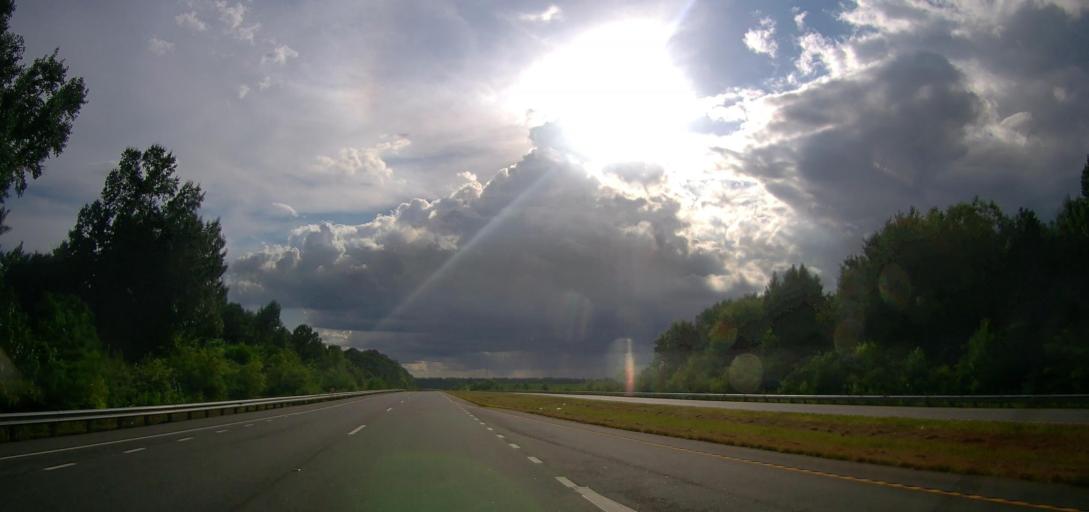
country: US
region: Georgia
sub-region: Peach County
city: Fort Valley
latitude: 32.5709
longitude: -83.9171
